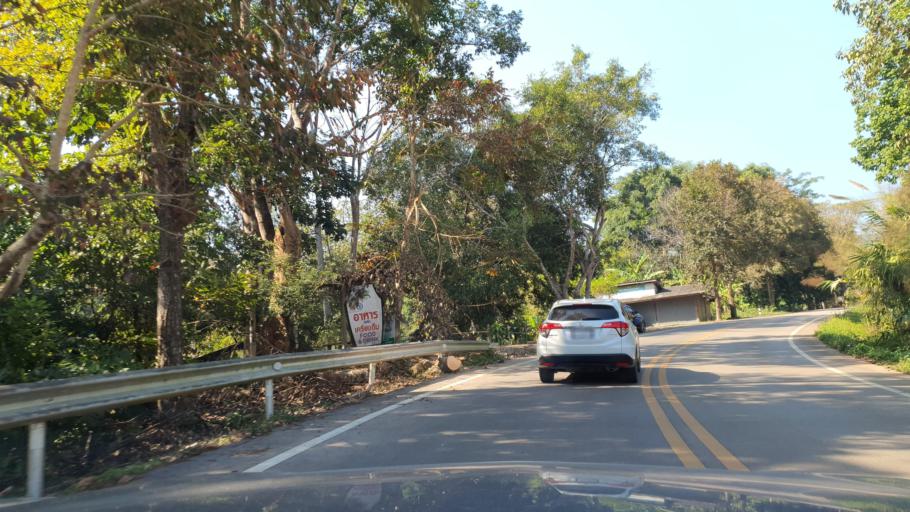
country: TH
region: Chiang Rai
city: Mae Lao
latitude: 19.8620
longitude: 99.6519
